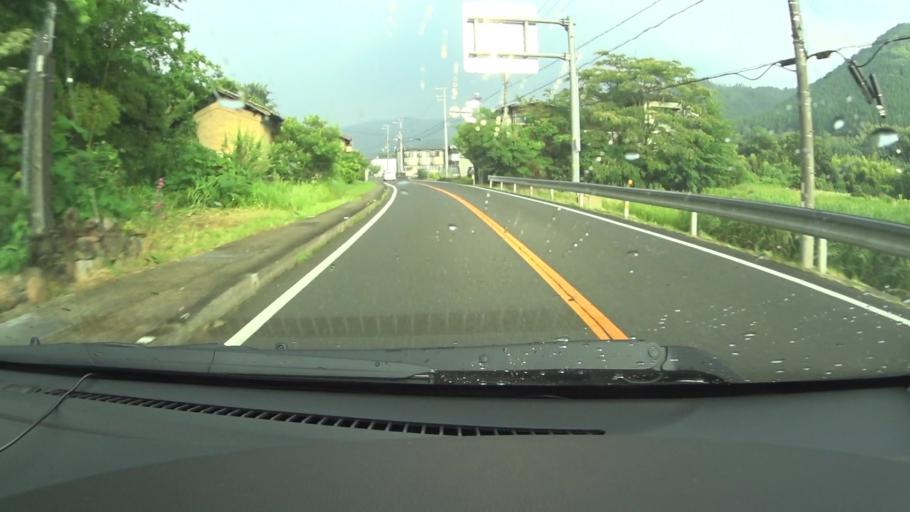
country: JP
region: Kyoto
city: Ayabe
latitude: 35.2921
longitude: 135.2704
